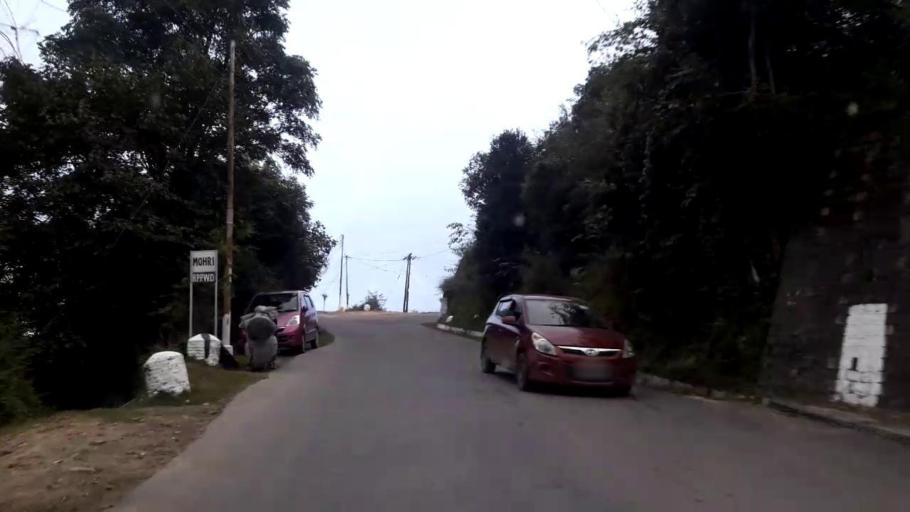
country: IN
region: Himachal Pradesh
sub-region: Shimla
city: Jutogh
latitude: 31.0472
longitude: 77.1349
